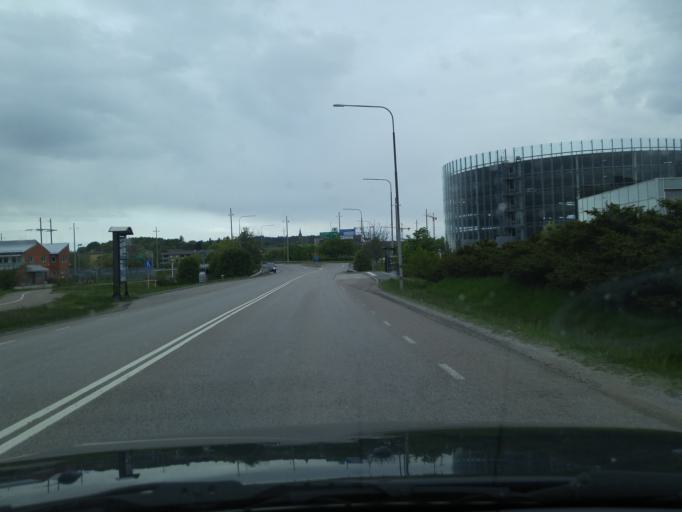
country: SE
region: Vaestra Goetaland
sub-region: Molndal
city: Moelndal
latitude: 57.6431
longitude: 12.0179
